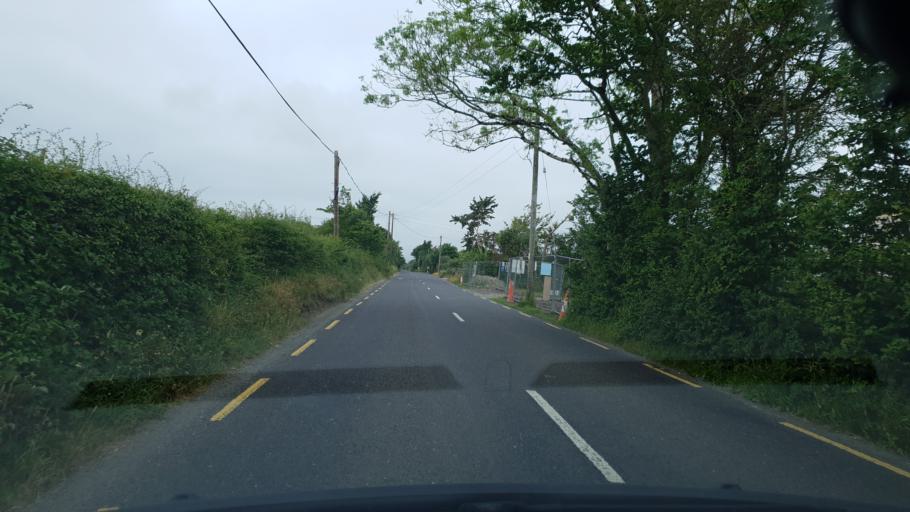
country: IE
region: Munster
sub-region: Ciarrai
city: Tralee
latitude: 52.1636
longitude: -9.6171
